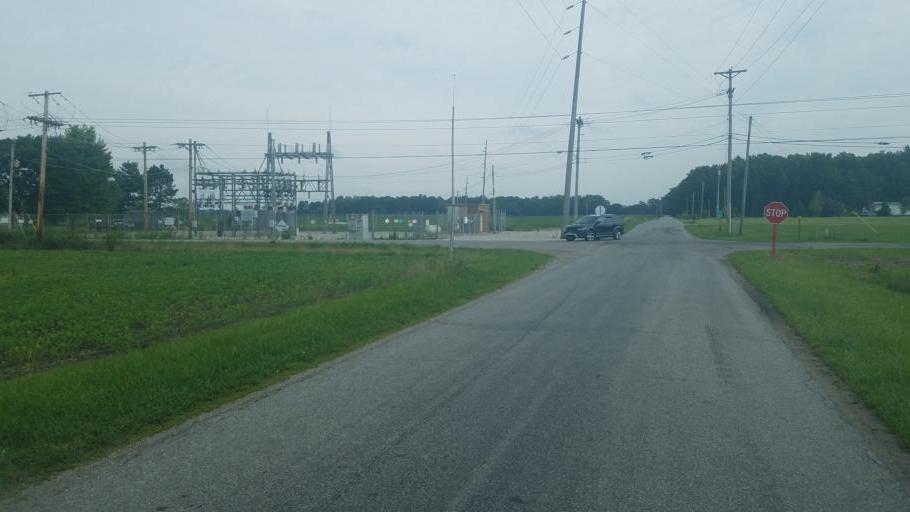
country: US
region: Ohio
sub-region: Delaware County
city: Ashley
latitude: 40.4216
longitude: -82.9093
